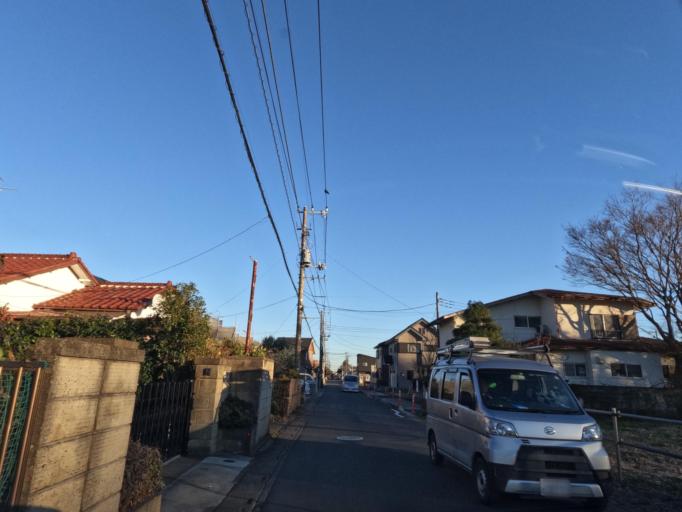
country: JP
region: Saitama
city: Iwatsuki
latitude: 35.9612
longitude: 139.6842
